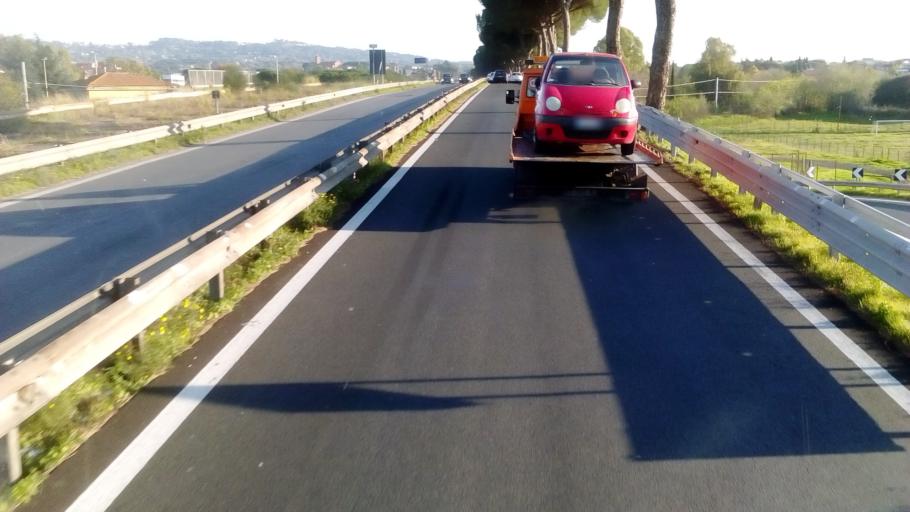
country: IT
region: Latium
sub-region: Citta metropolitana di Roma Capitale
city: Ciampino
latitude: 41.7782
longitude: 12.6056
